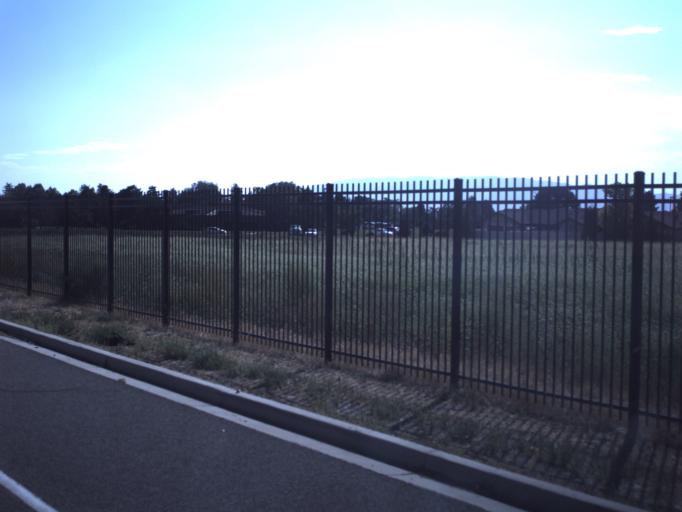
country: US
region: Utah
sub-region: Utah County
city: Cedar Hills
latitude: 40.4009
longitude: -111.7734
